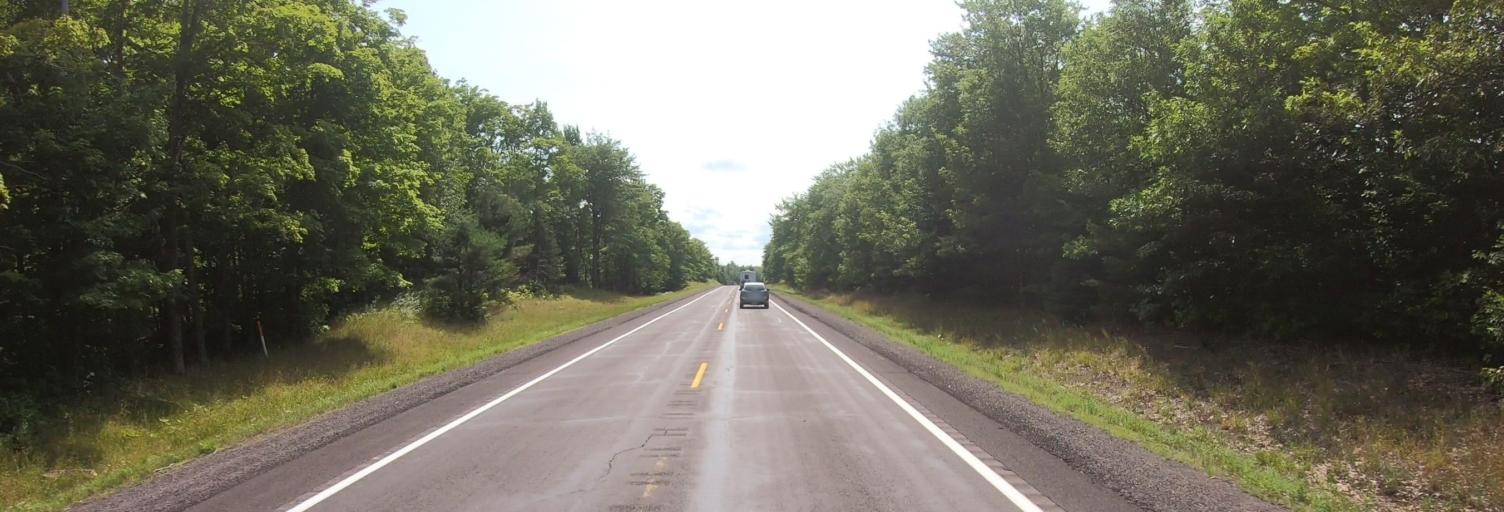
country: US
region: Michigan
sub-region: Ontonagon County
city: Ontonagon
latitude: 46.8628
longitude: -88.9072
